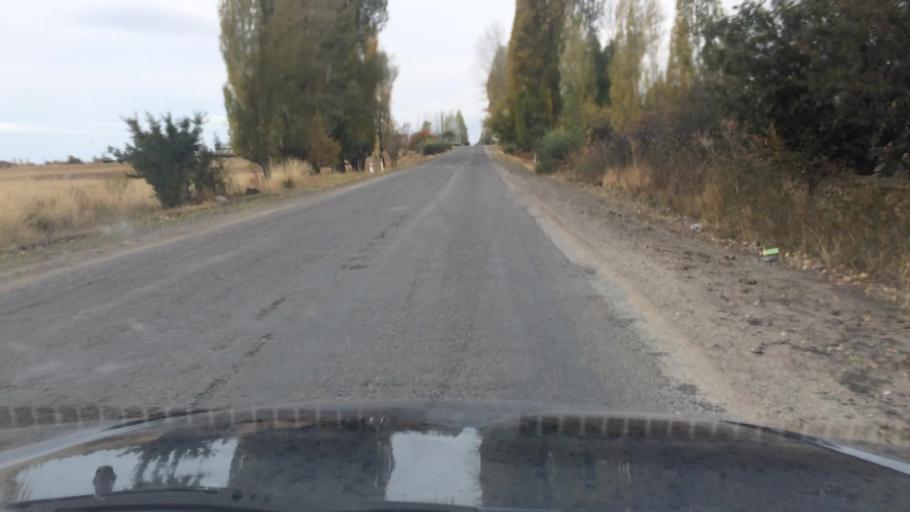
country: KG
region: Ysyk-Koel
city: Pokrovka
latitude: 42.7366
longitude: 77.9531
